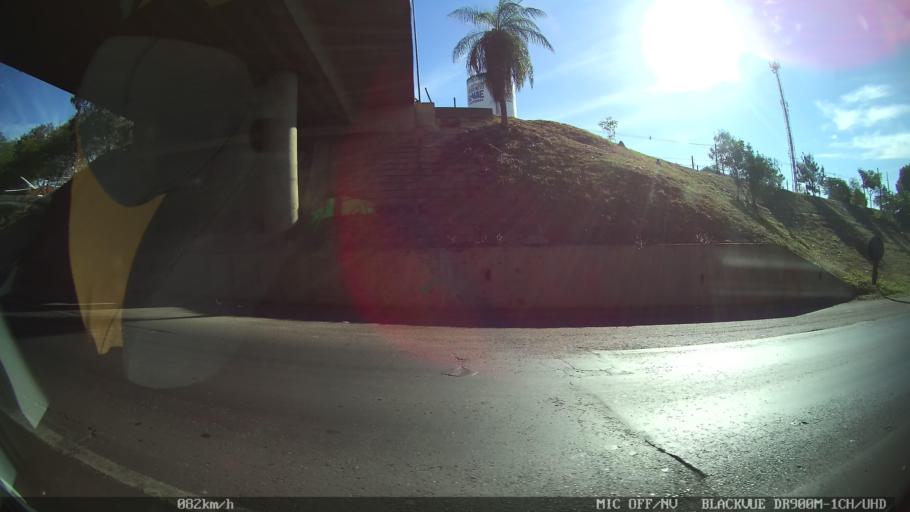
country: BR
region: Sao Paulo
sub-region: Sao Jose Do Rio Preto
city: Sao Jose do Rio Preto
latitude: -20.8170
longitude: -49.3573
